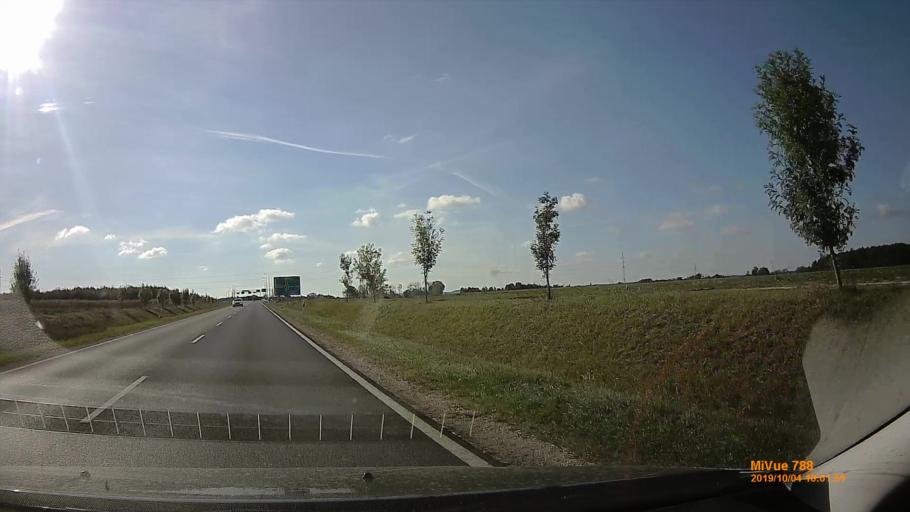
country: HU
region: Somogy
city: Kaposvar
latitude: 46.4022
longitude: 17.7748
